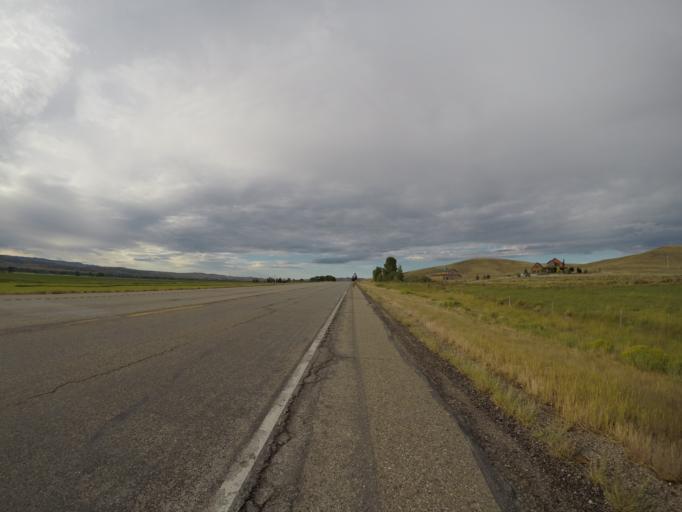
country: US
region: Wyoming
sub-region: Carbon County
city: Saratoga
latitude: 41.3803
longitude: -106.7495
